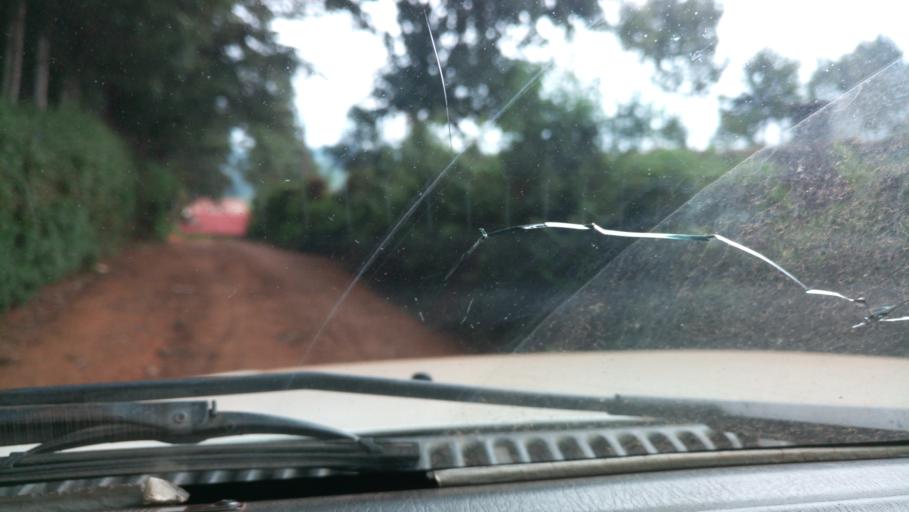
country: KE
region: Nyeri
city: Othaya
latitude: -0.6031
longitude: 36.8421
